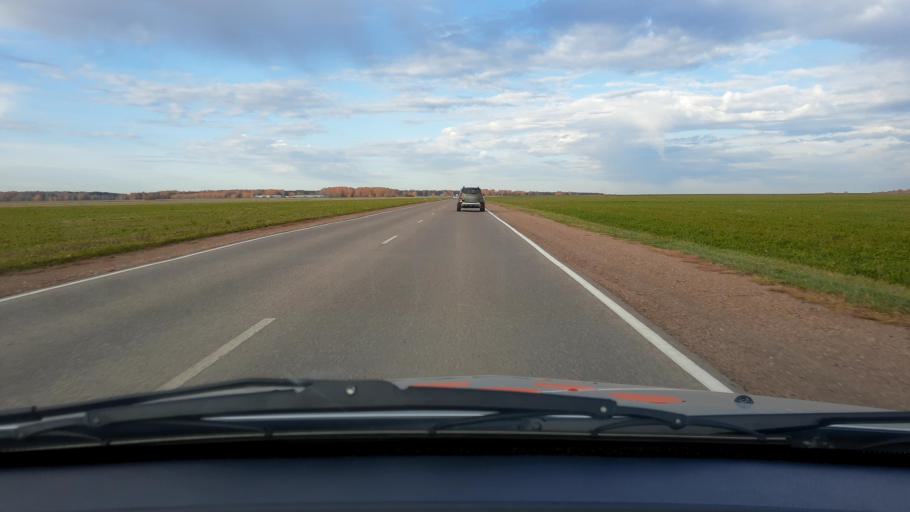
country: RU
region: Bashkortostan
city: Avdon
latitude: 54.8216
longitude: 55.6769
